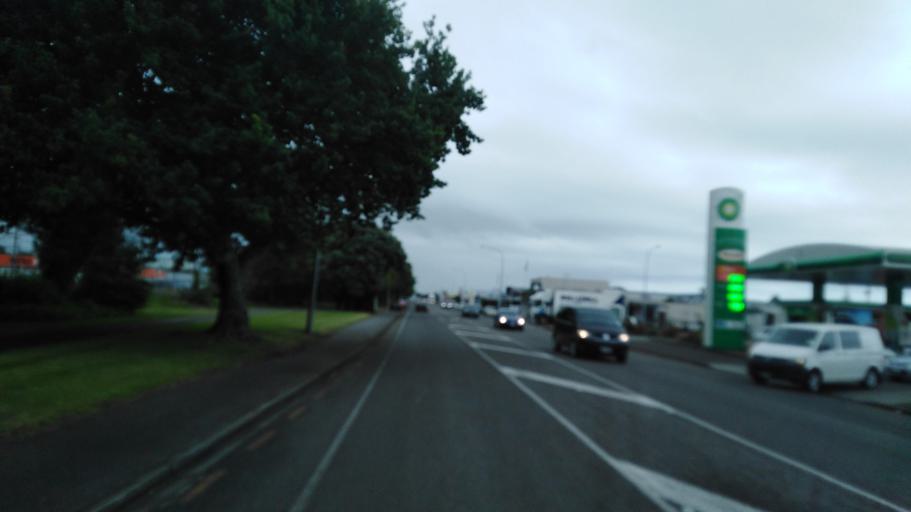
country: NZ
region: Manawatu-Wanganui
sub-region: Horowhenua District
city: Levin
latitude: -40.6295
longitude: 175.2793
